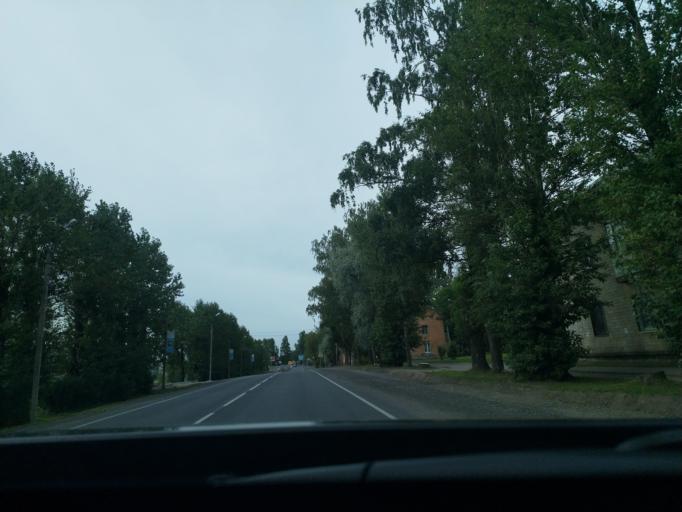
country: RU
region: Leningrad
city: Nikol'skoye
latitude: 59.7050
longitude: 30.7844
